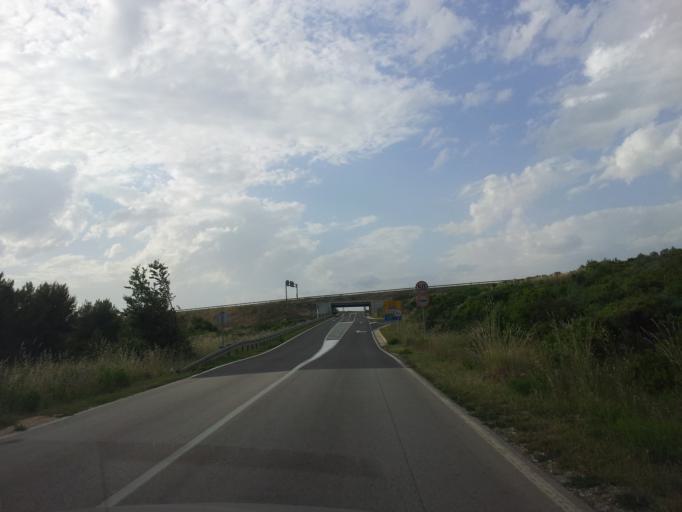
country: HR
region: Zadarska
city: Sukosan
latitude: 44.0691
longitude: 15.3400
